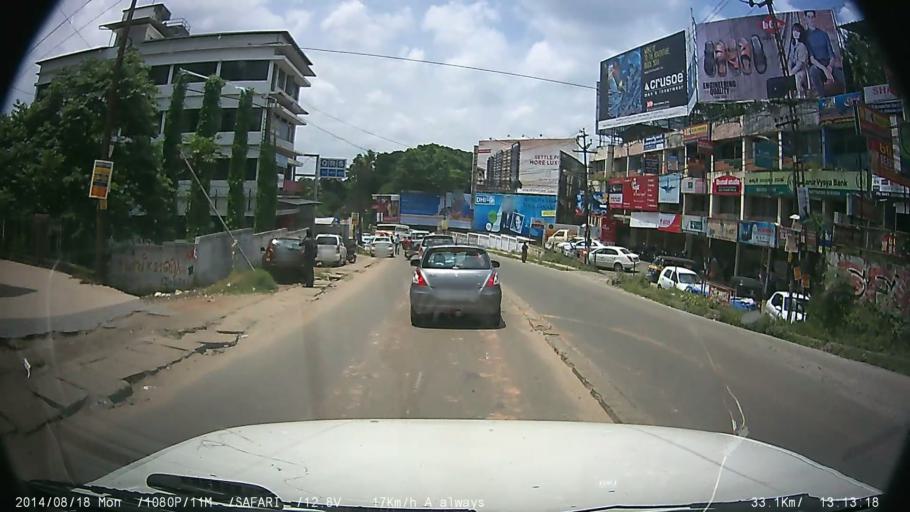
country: IN
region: Kerala
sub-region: Kottayam
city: Kottayam
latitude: 9.5935
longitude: 76.5229
